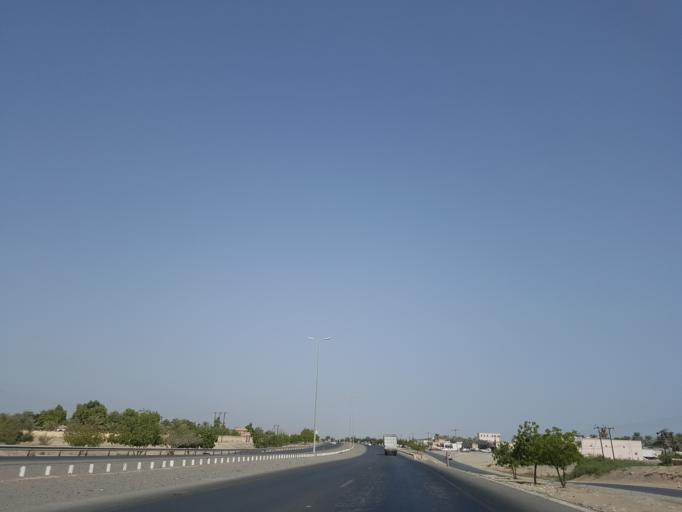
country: OM
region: Al Batinah
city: As Suwayq
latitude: 23.7510
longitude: 57.6131
